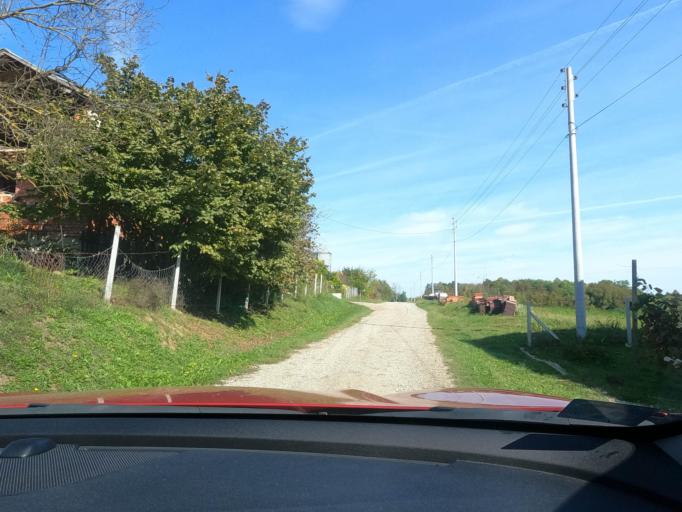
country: HR
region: Sisacko-Moslavacka
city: Glina
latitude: 45.3338
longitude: 16.2083
